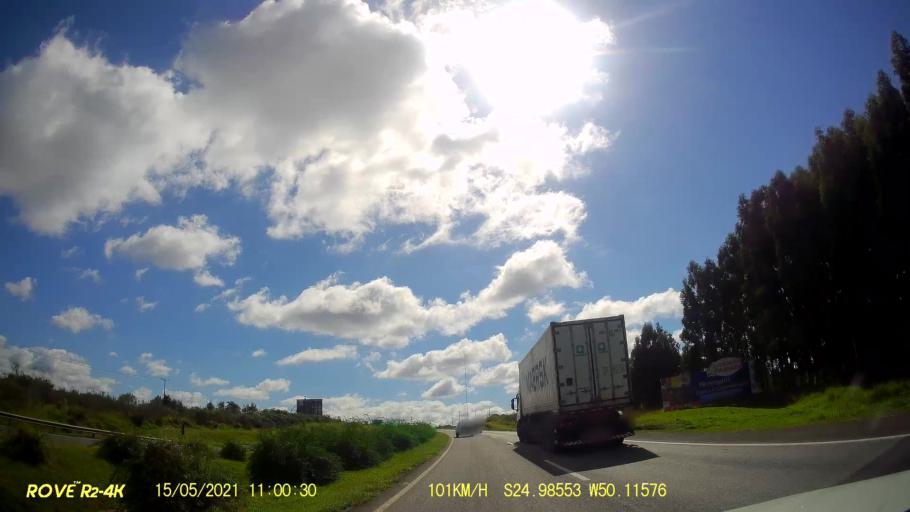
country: BR
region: Parana
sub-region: Carambei
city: Carambei
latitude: -24.9857
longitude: -50.1160
